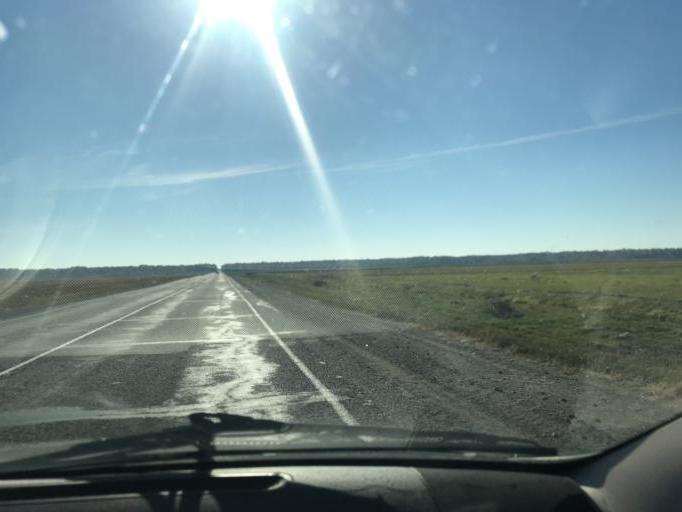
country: BY
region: Minsk
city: Starobin
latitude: 52.5216
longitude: 27.4741
